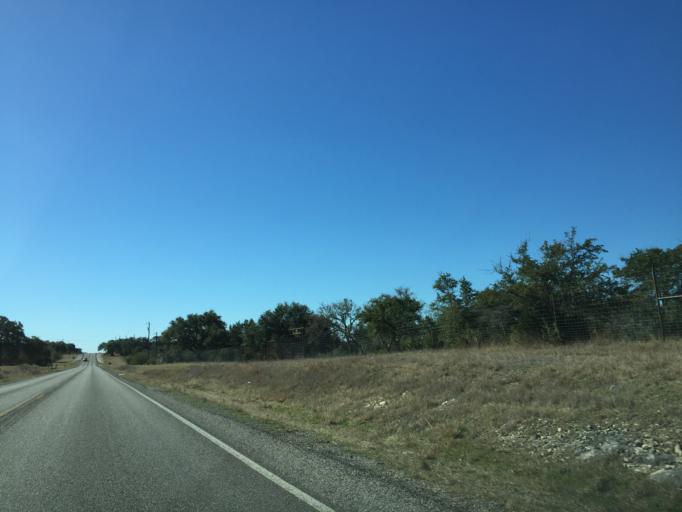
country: US
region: Texas
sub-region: Comal County
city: Garden Ridge
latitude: 29.7322
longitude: -98.3071
